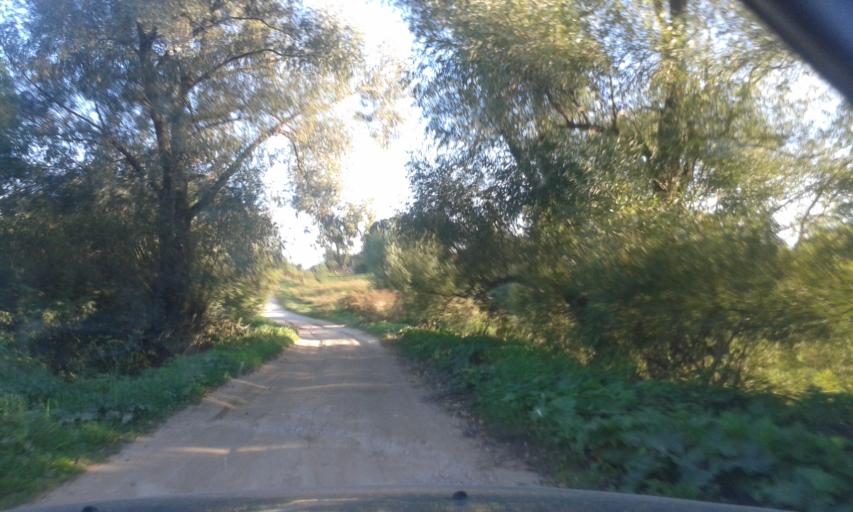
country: RU
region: Tula
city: Dubna
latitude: 54.1366
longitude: 37.1517
